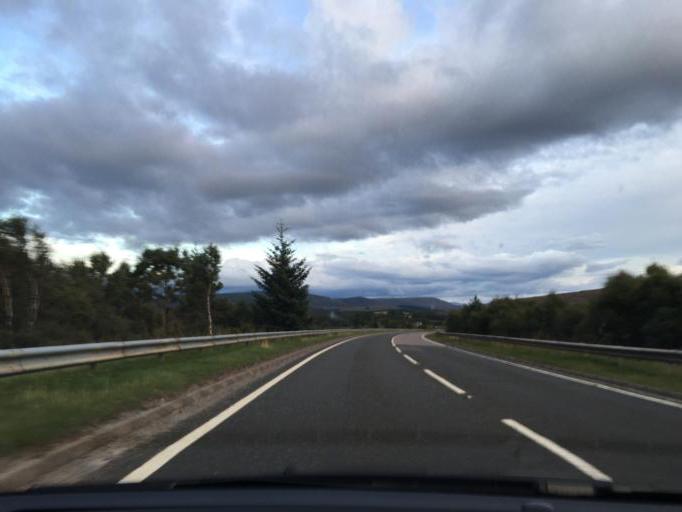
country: GB
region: Scotland
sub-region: Highland
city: Inverness
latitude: 57.3723
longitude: -4.0292
